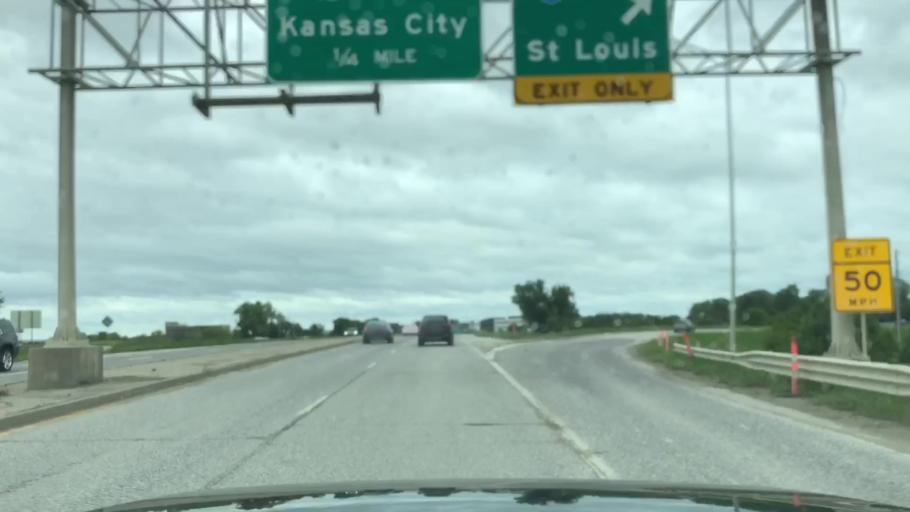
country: US
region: Missouri
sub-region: Saint Charles County
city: Saint Charles
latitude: 38.7521
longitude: -90.4607
